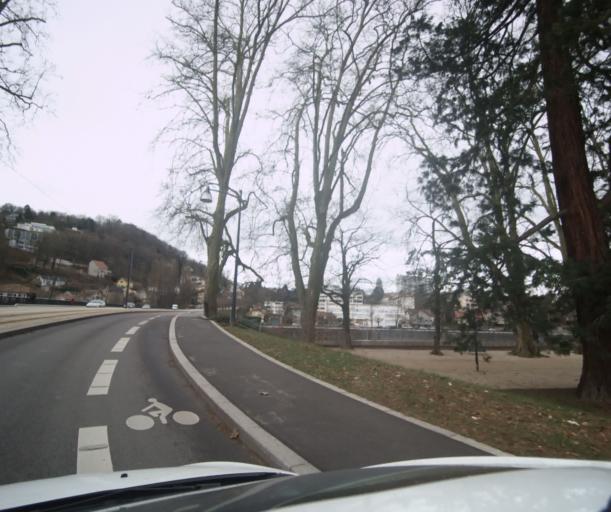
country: FR
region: Franche-Comte
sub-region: Departement du Doubs
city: Besancon
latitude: 47.2317
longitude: 6.0186
